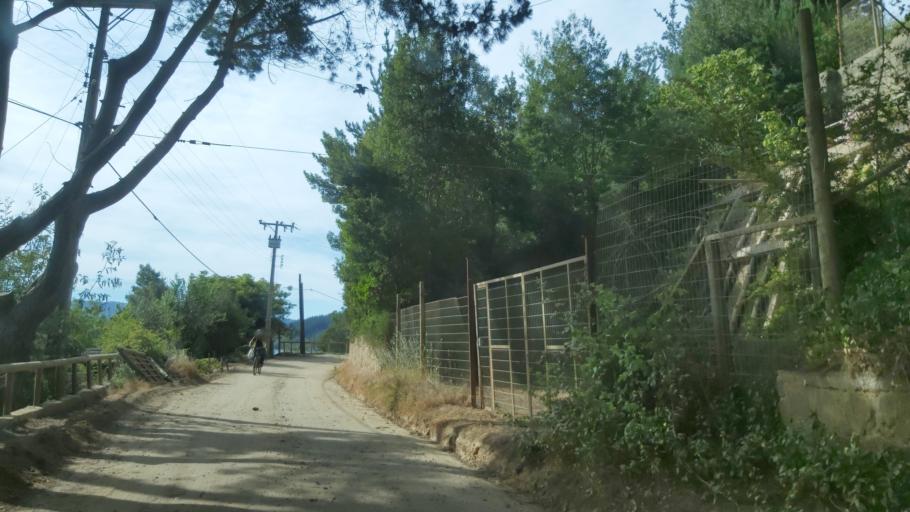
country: CL
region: Maule
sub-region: Provincia de Talca
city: Constitucion
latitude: -34.8424
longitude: -72.0409
